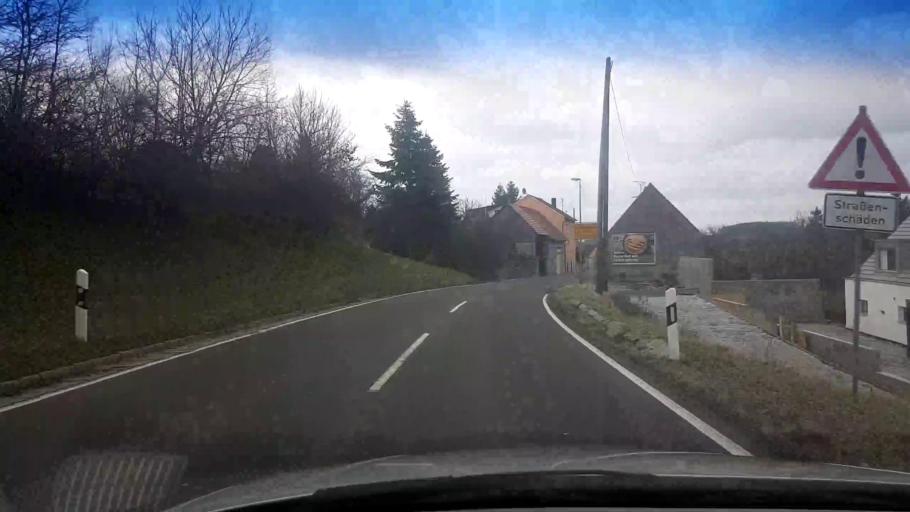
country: DE
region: Bavaria
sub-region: Regierungsbezirk Unterfranken
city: Eltmann
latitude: 49.9327
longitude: 10.6487
